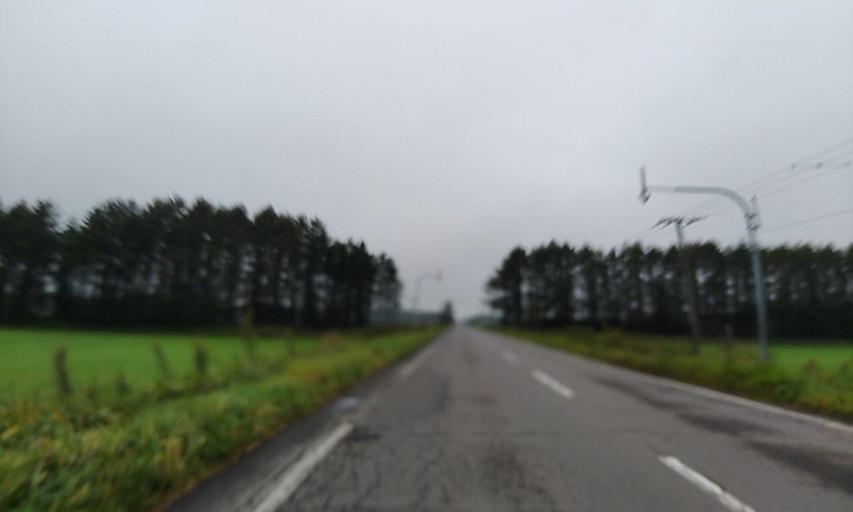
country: JP
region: Hokkaido
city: Shibetsu
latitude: 43.5138
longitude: 144.6751
